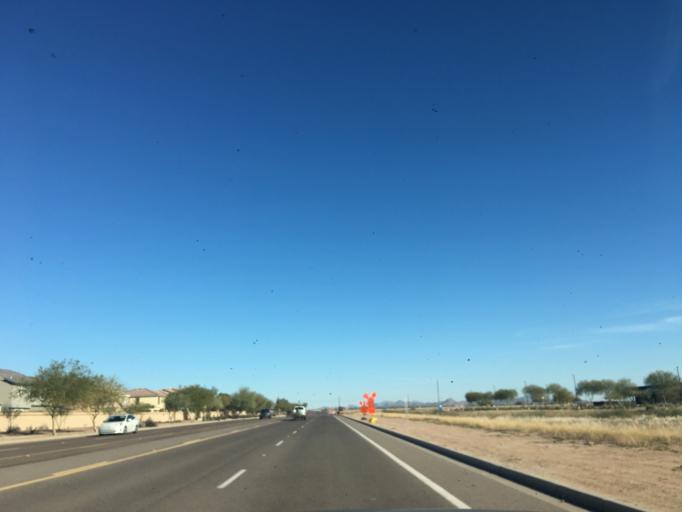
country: US
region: Arizona
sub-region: Pinal County
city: Maricopa
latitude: 33.0436
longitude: -112.0041
